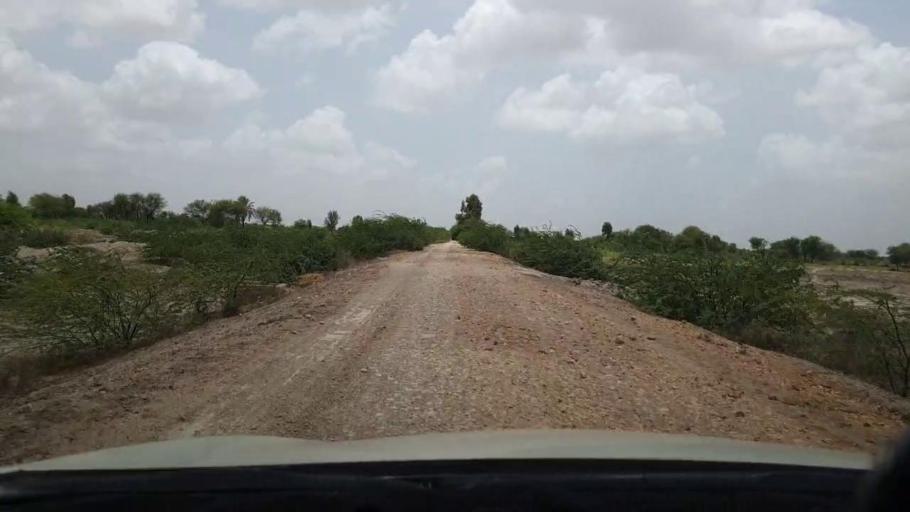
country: PK
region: Sindh
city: Kadhan
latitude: 24.3768
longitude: 68.9291
